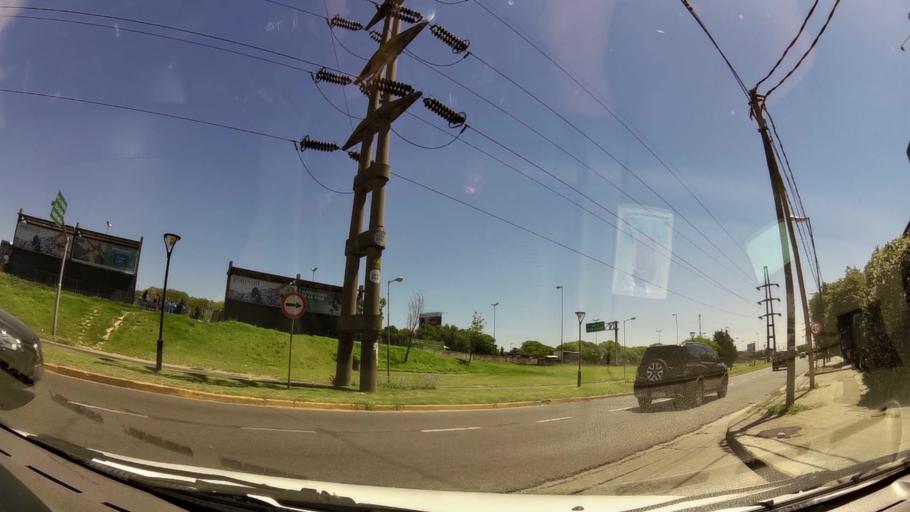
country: AR
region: Buenos Aires
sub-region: Partido de San Isidro
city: San Isidro
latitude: -34.5042
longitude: -58.5370
